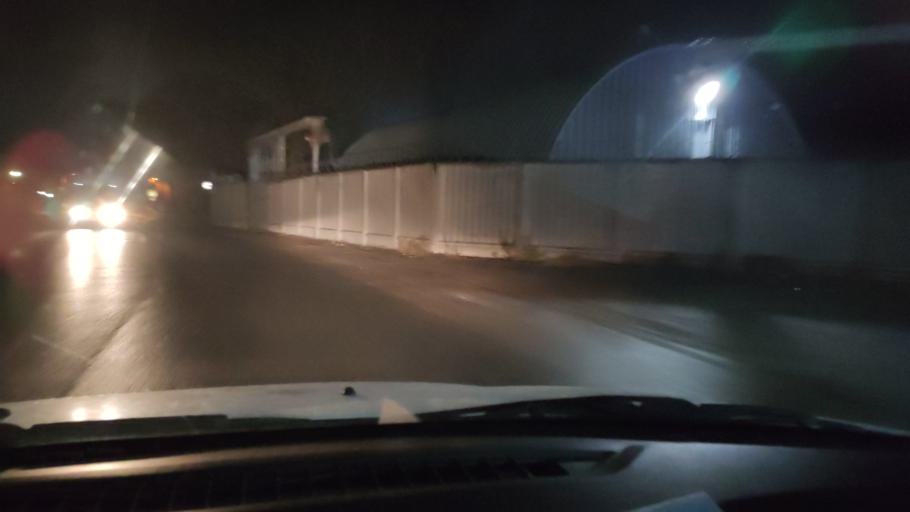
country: RU
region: Perm
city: Overyata
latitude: 58.0204
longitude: 55.9158
